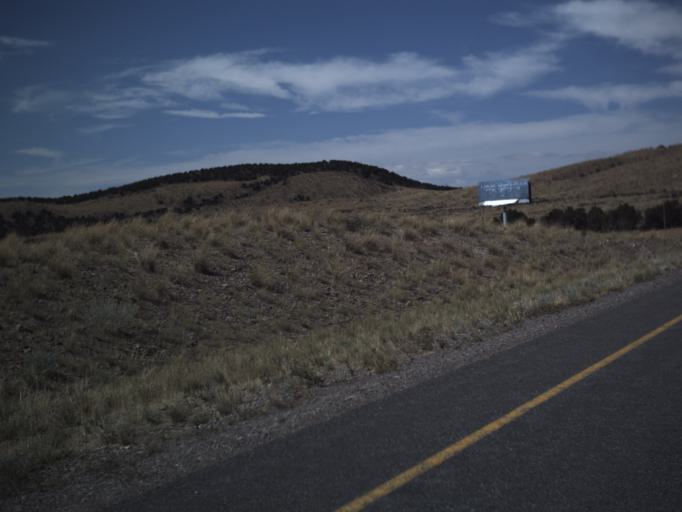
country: US
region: Utah
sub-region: Beaver County
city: Beaver
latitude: 38.6176
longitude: -112.6081
